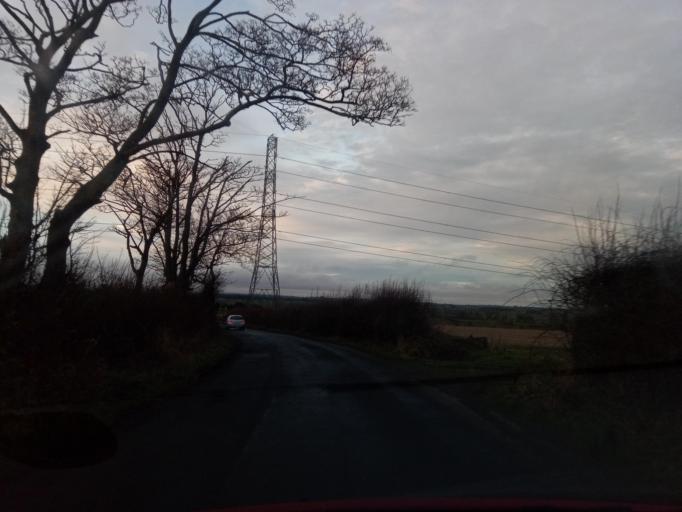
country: GB
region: England
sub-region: Northumberland
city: Ponteland
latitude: 55.0781
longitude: -1.7364
